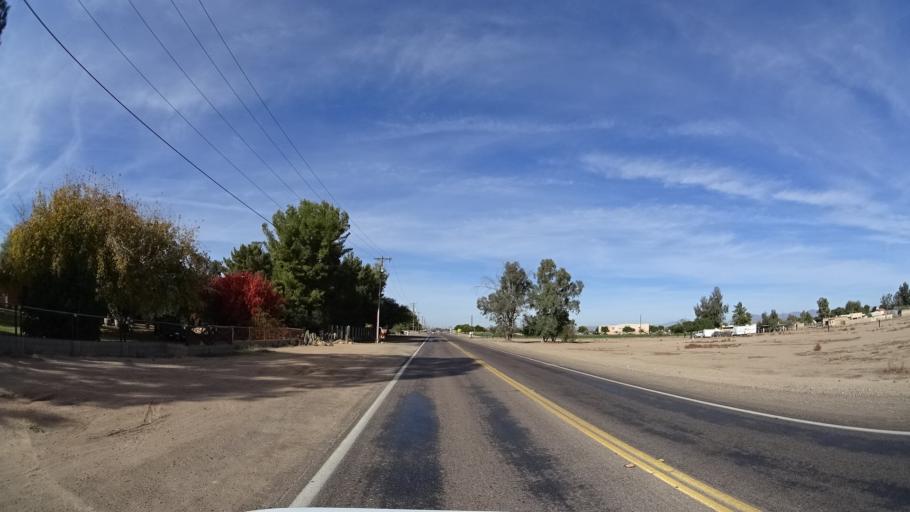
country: US
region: Arizona
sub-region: Maricopa County
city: Queen Creek
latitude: 33.2369
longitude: -111.6859
